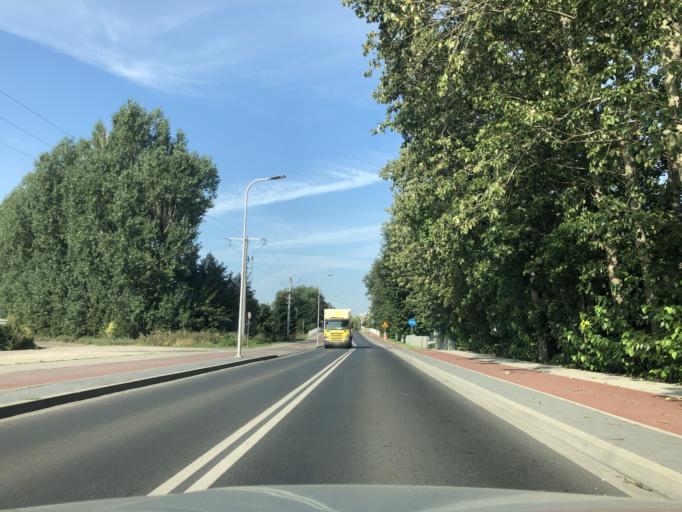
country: PL
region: Greater Poland Voivodeship
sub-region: Powiat pilski
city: Pila
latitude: 53.1477
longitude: 16.7679
